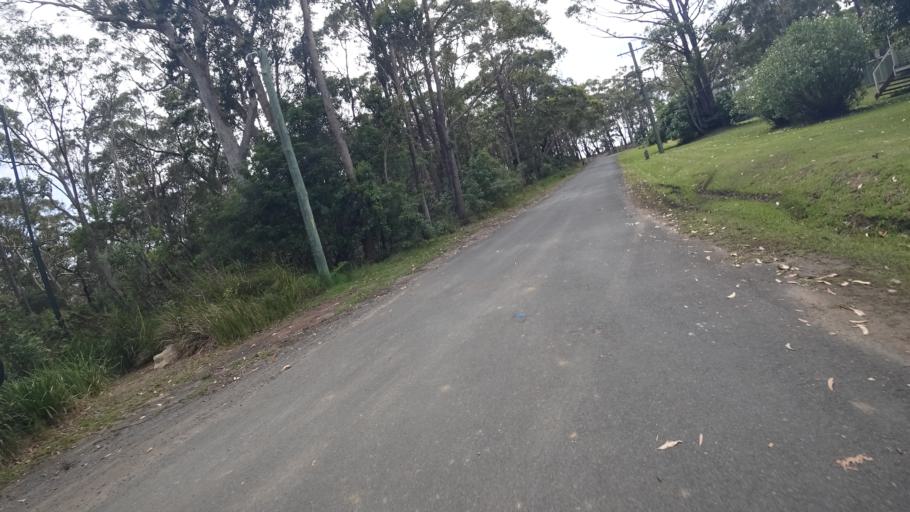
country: AU
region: New South Wales
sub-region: Shoalhaven Shire
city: Milton
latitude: -35.2335
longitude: 150.5277
